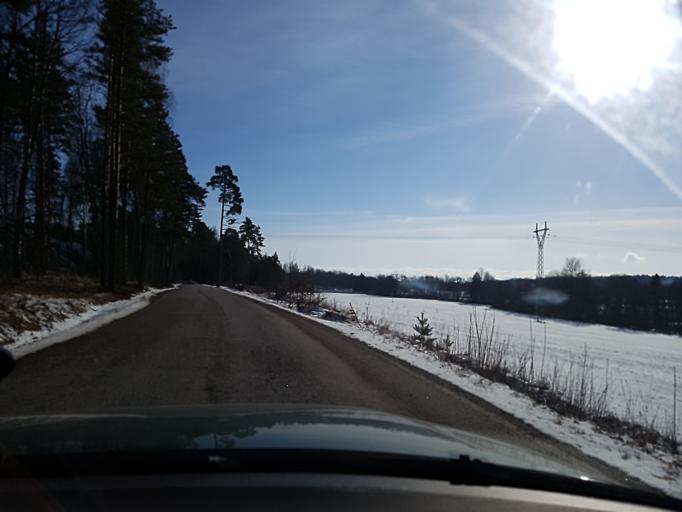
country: FI
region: Uusimaa
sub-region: Helsinki
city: Siuntio
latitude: 60.1043
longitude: 24.2925
